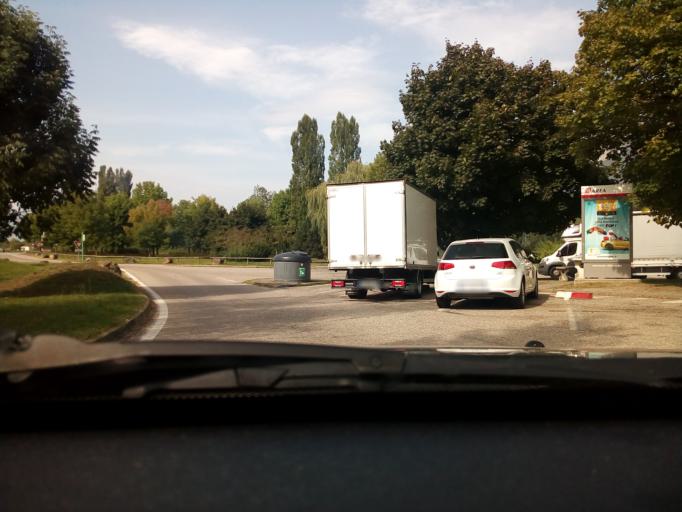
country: FR
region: Rhone-Alpes
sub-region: Departement de l'Isere
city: Saint-Nazaire-les-Eymes
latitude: 45.2472
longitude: 5.8674
